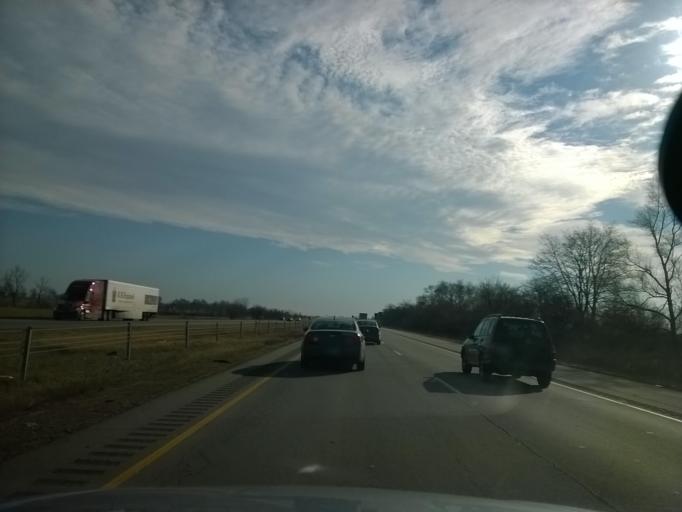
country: US
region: Indiana
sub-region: Johnson County
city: Edinburgh
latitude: 39.3720
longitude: -85.9427
